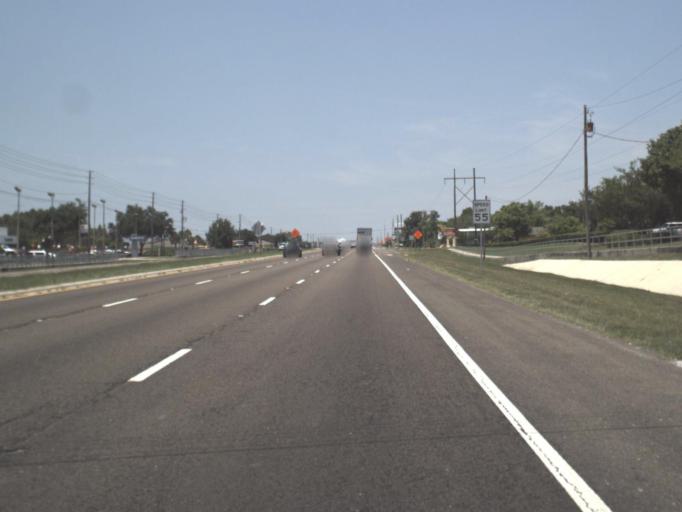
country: US
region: Florida
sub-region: Pasco County
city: Holiday
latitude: 28.1670
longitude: -82.7403
